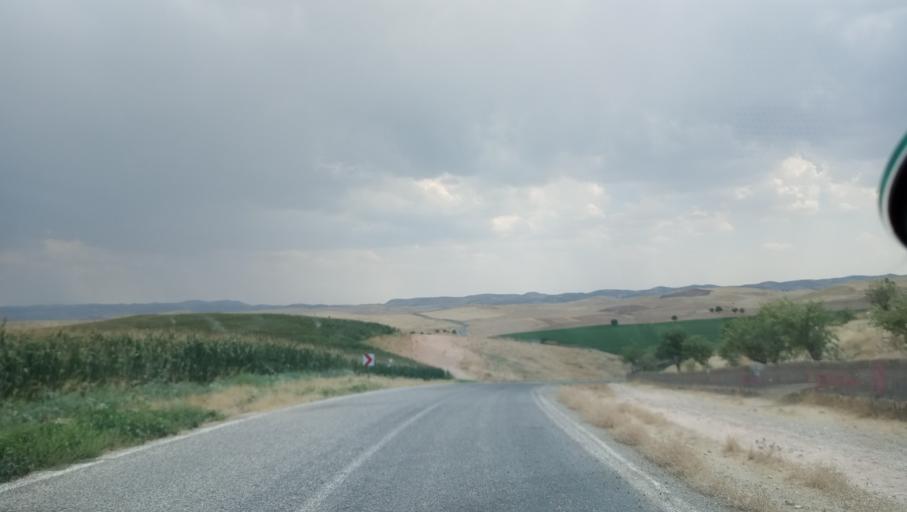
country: TR
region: Mardin
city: Baskavak
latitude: 37.6776
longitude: 40.8499
